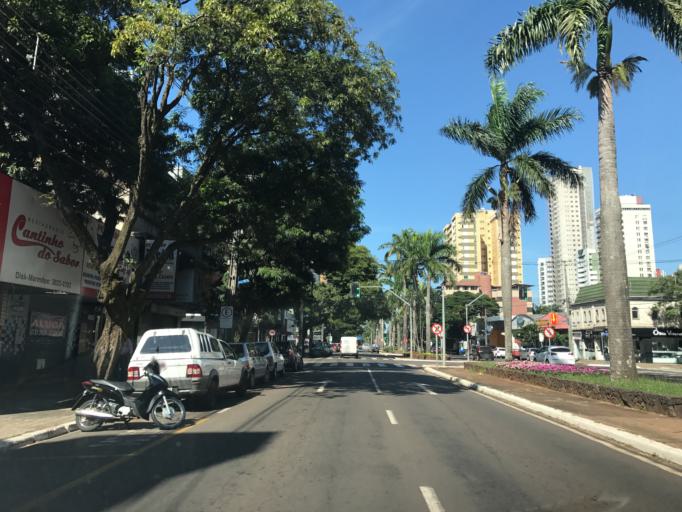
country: BR
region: Parana
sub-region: Maringa
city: Maringa
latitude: -23.4213
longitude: -51.9432
